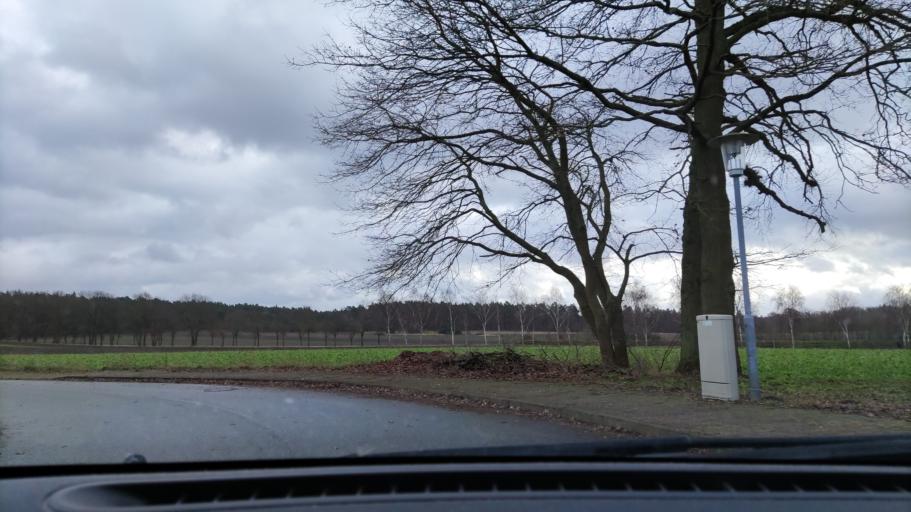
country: DE
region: Lower Saxony
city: Deutsch Evern
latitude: 53.2019
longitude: 10.4455
